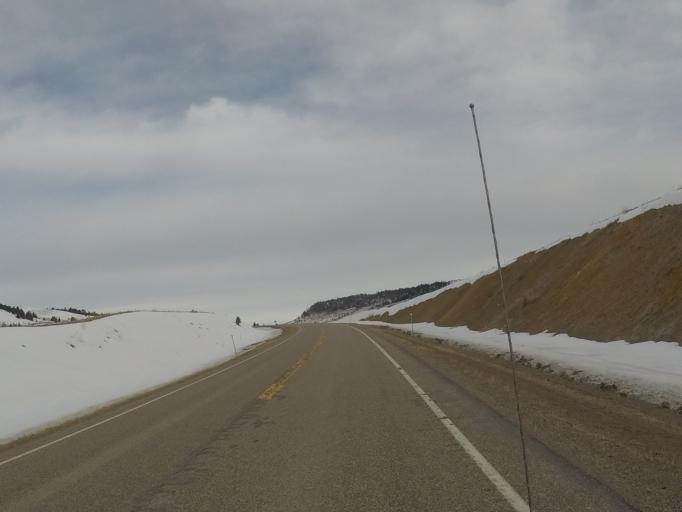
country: US
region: Montana
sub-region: Meagher County
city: White Sulphur Springs
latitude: 46.6369
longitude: -110.8716
